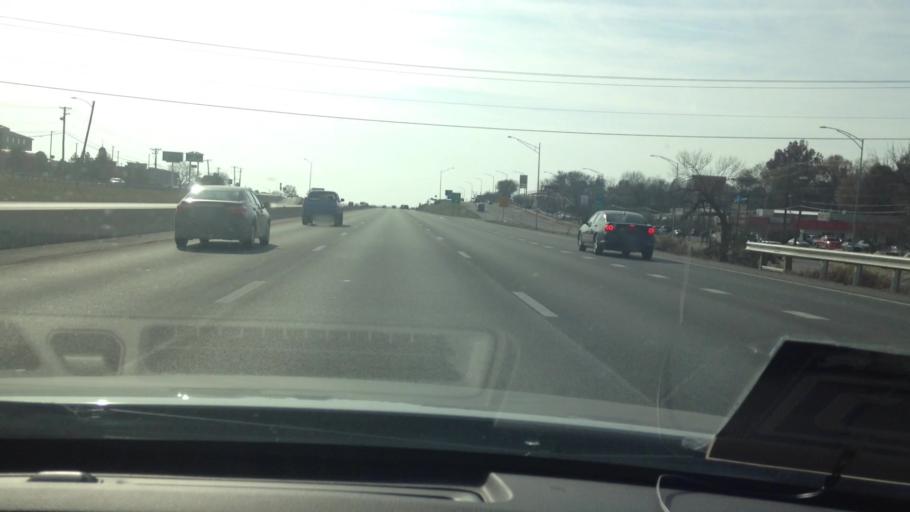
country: US
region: Missouri
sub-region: Jackson County
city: Grandview
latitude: 38.8953
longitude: -94.5248
